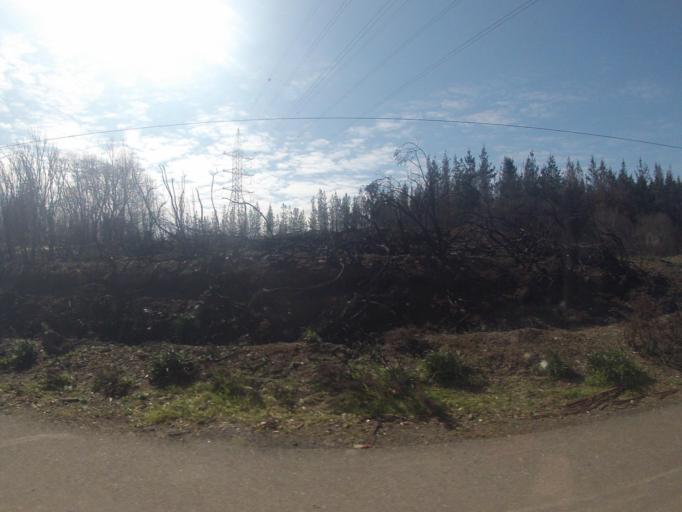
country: CL
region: Araucania
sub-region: Provincia de Malleco
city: Victoria
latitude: -38.1499
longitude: -72.3063
